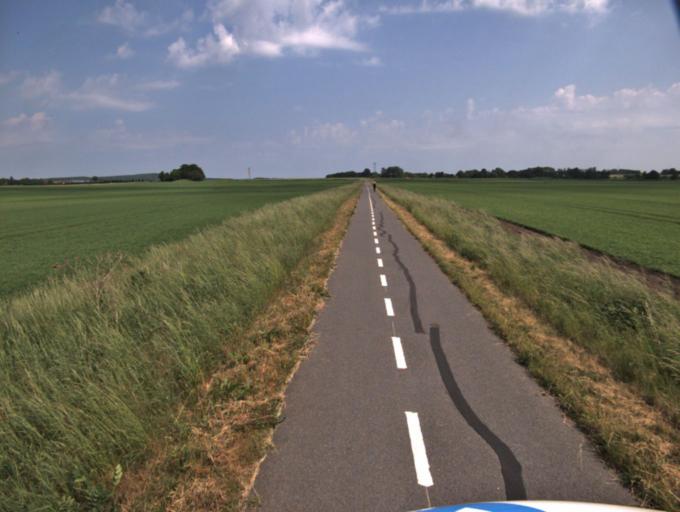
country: SE
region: Skane
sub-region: Kristianstads Kommun
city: Kristianstad
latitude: 56.0655
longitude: 14.1901
